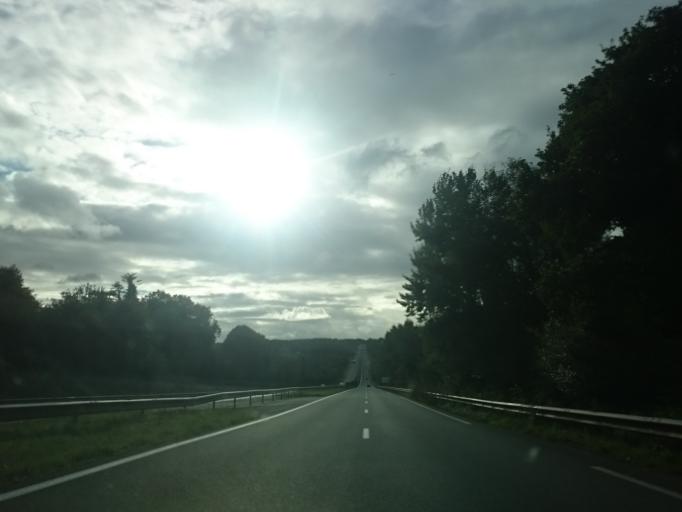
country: FR
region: Brittany
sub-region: Departement des Cotes-d'Armor
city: Belle-Isle-en-Terre
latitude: 48.5509
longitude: -3.3918
